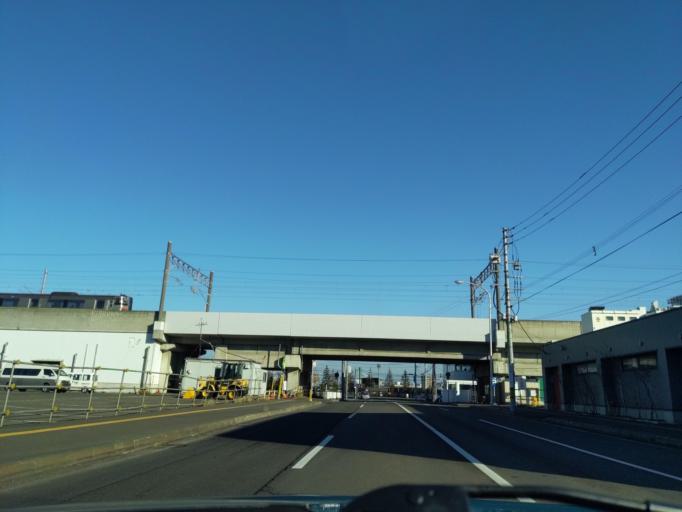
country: JP
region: Hokkaido
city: Sapporo
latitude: 43.0739
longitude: 141.3231
